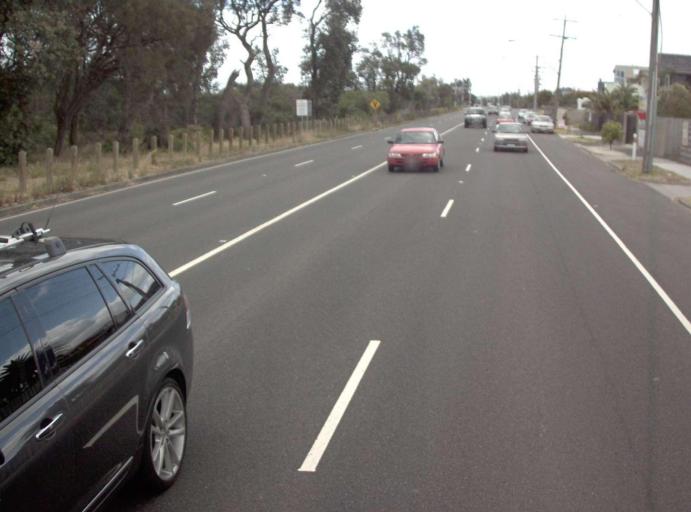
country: AU
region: Victoria
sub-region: Kingston
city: Carrum
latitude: -38.0880
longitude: 145.1250
